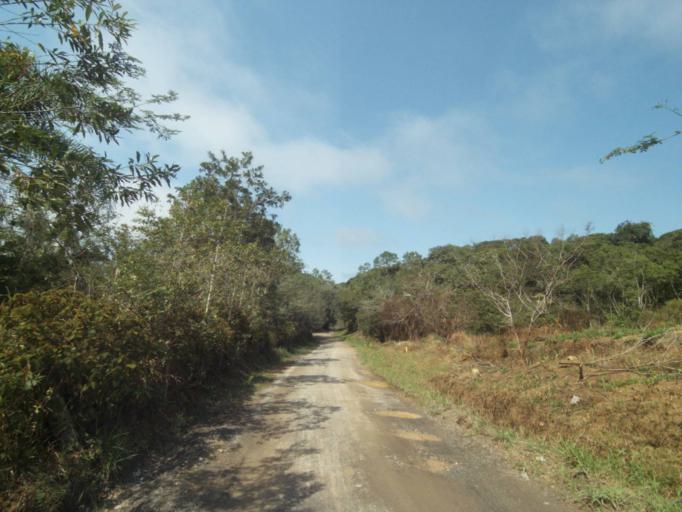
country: BR
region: Parana
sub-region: Paranagua
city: Paranagua
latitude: -25.5562
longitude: -48.6477
